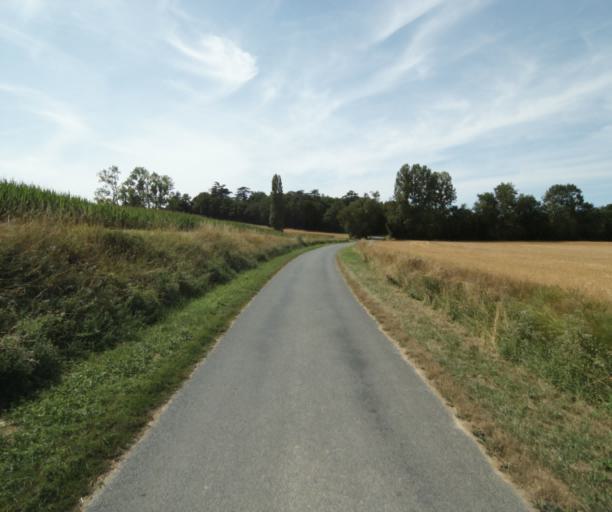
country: FR
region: Midi-Pyrenees
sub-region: Departement du Tarn
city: Soreze
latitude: 43.5122
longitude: 2.0418
